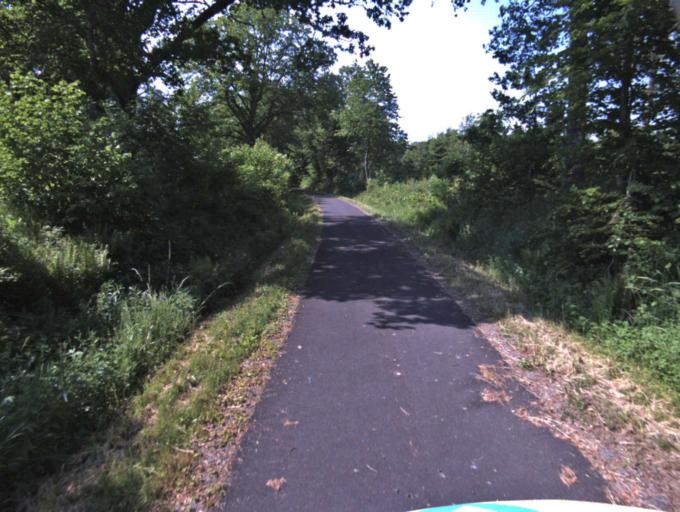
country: SE
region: Skane
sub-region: Kristianstads Kommun
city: Tollarp
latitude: 56.1981
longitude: 14.2884
